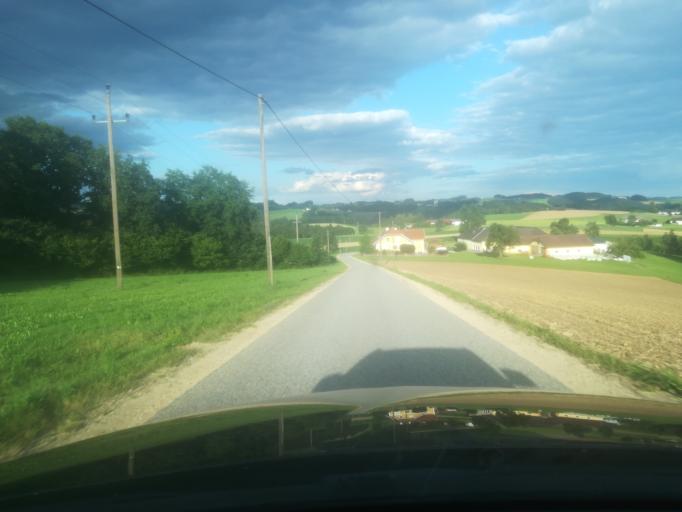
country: AT
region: Upper Austria
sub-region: Politischer Bezirk Urfahr-Umgebung
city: Engerwitzdorf
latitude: 48.3654
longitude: 14.5600
